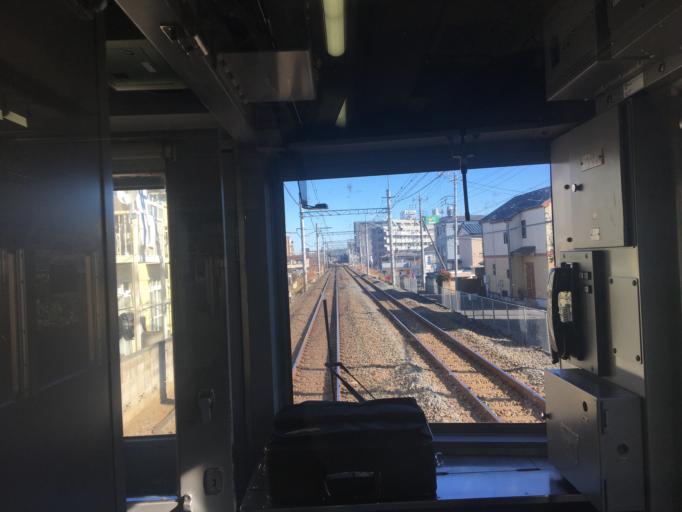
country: JP
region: Saitama
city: Iwatsuki
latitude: 35.9464
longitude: 139.6882
